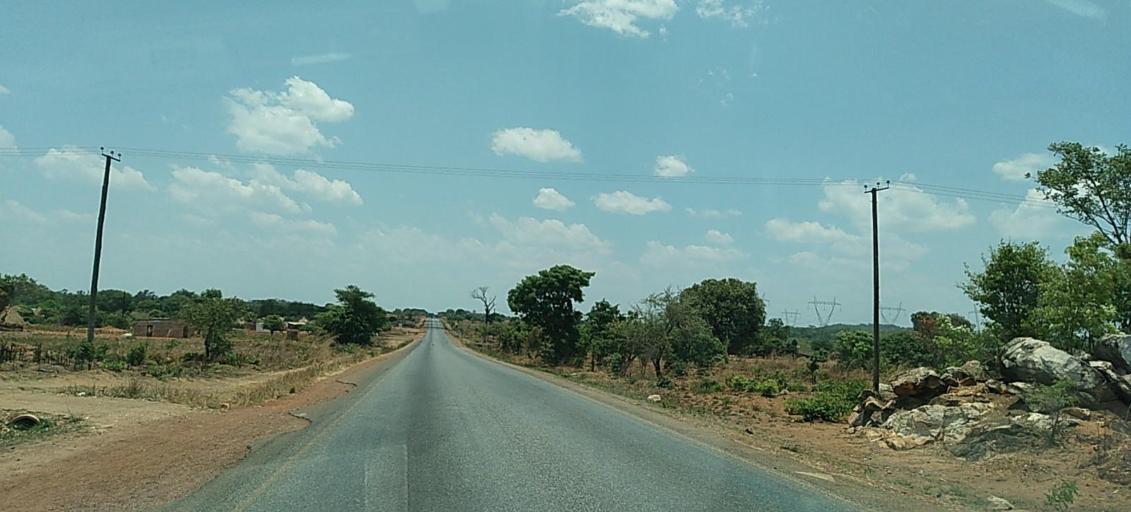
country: ZM
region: Central
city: Kapiri Mposhi
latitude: -13.6999
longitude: 28.6287
